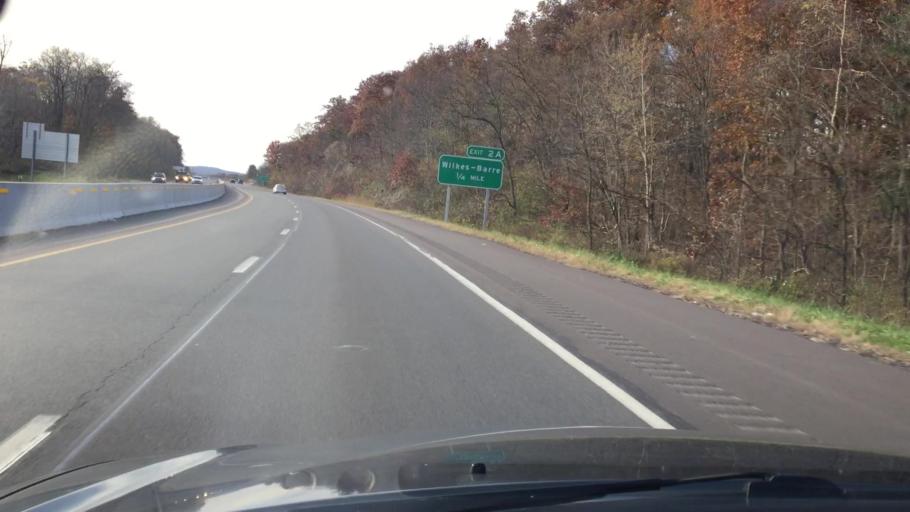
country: US
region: Pennsylvania
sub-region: Luzerne County
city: Ashley
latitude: 41.2032
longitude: -75.9341
